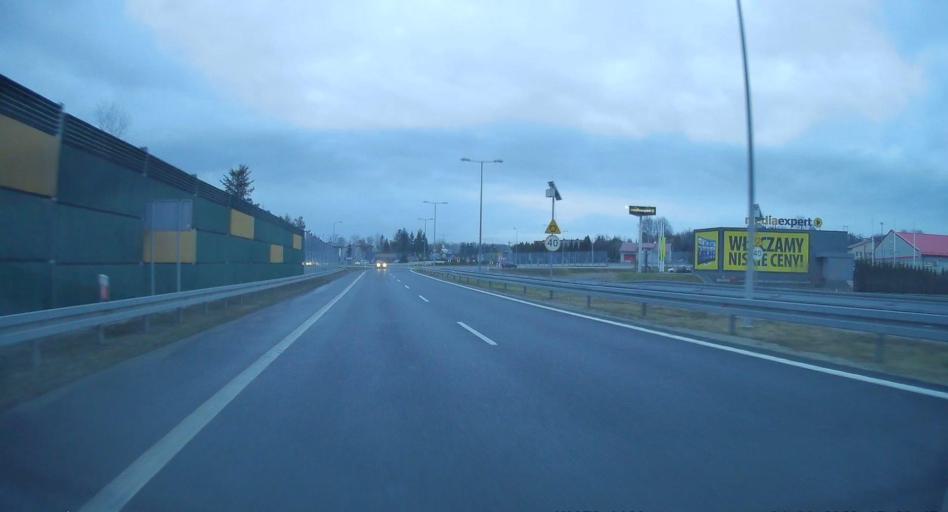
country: PL
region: Subcarpathian Voivodeship
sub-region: Powiat ropczycko-sedziszowski
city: Ropczyce
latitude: 50.0562
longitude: 21.6303
